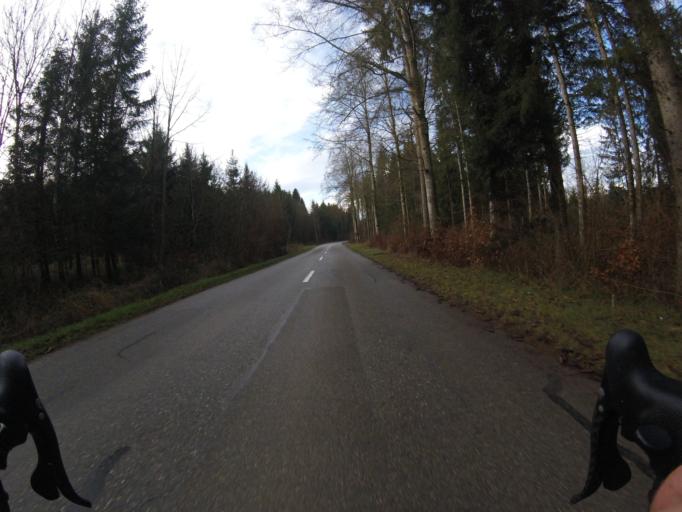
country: CH
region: Fribourg
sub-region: Sense District
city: Flamatt
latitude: 46.9096
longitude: 7.3334
